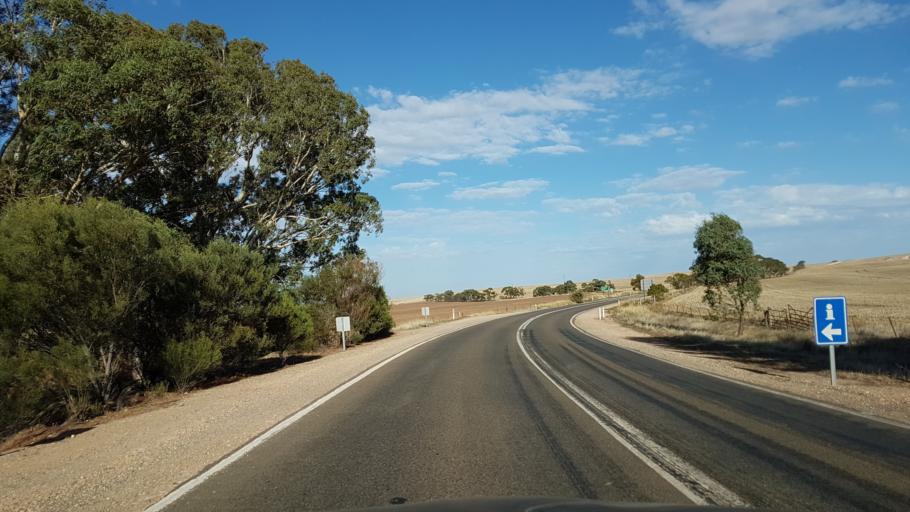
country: AU
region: South Australia
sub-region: Clare and Gilbert Valleys
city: Clare
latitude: -33.6917
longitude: 138.4577
